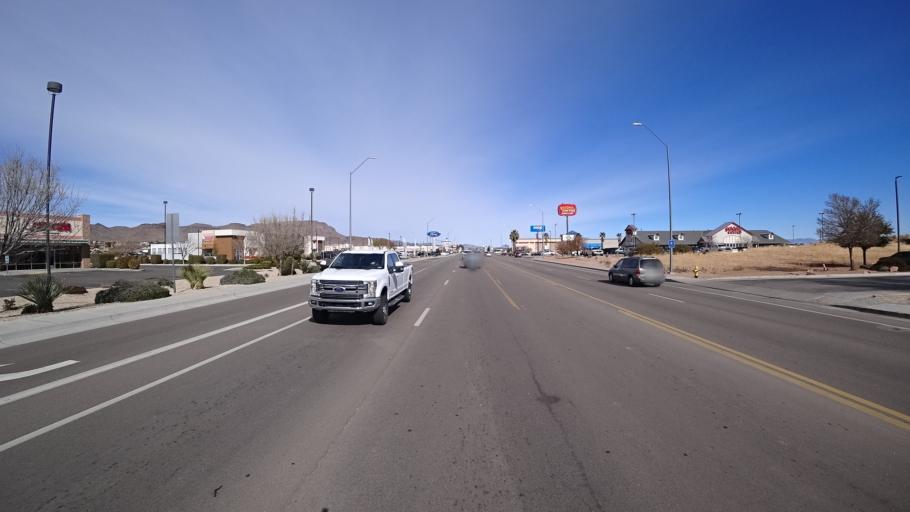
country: US
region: Arizona
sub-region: Mohave County
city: New Kingman-Butler
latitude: 35.2257
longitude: -114.0364
